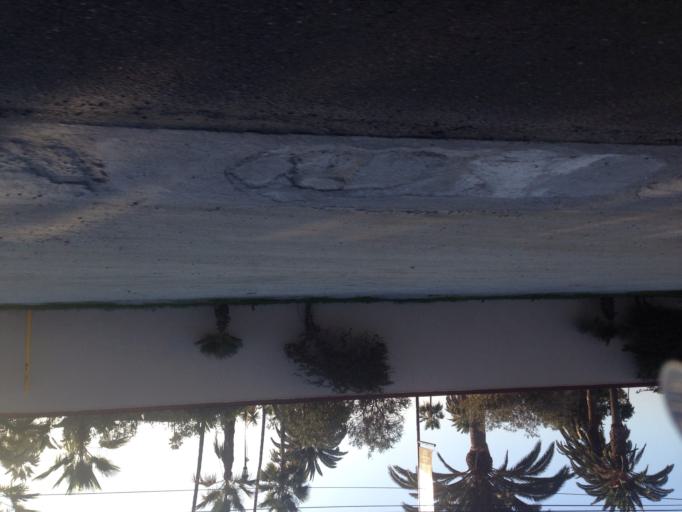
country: MX
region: Baja California
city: El Sauzal
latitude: 31.8645
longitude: -116.6574
